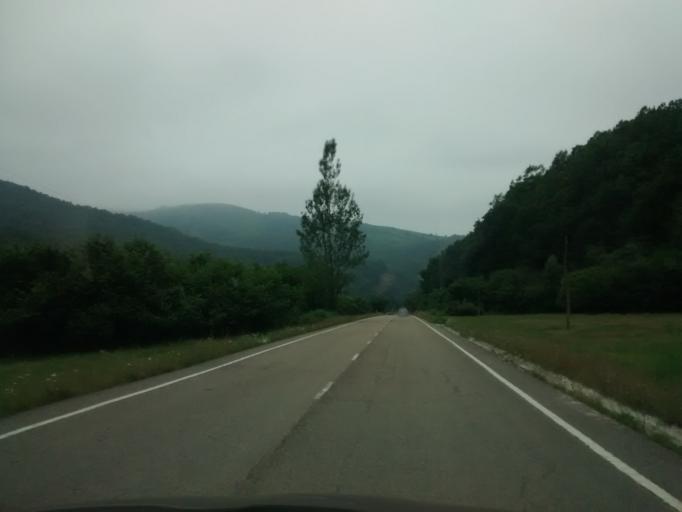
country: ES
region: Cantabria
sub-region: Provincia de Cantabria
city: Ruente
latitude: 43.1481
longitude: -4.2046
